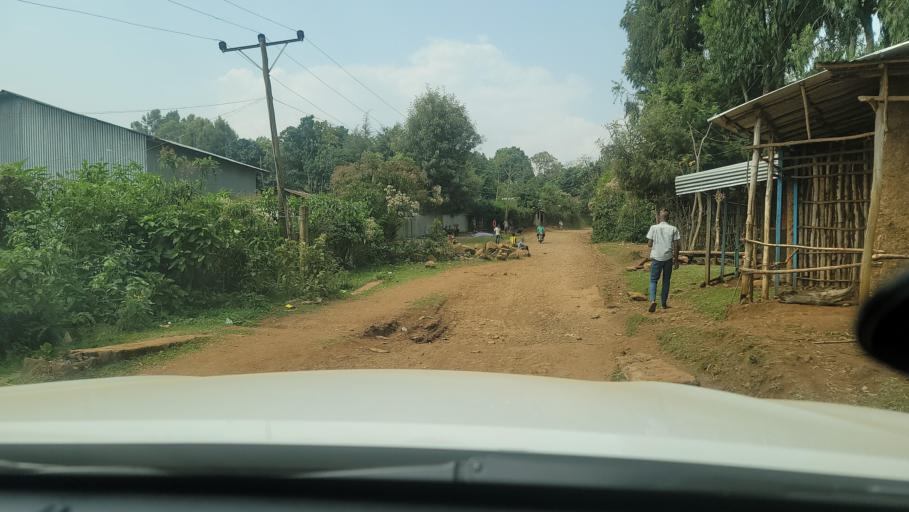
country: ET
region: Oromiya
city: Agaro
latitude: 7.8113
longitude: 36.4725
